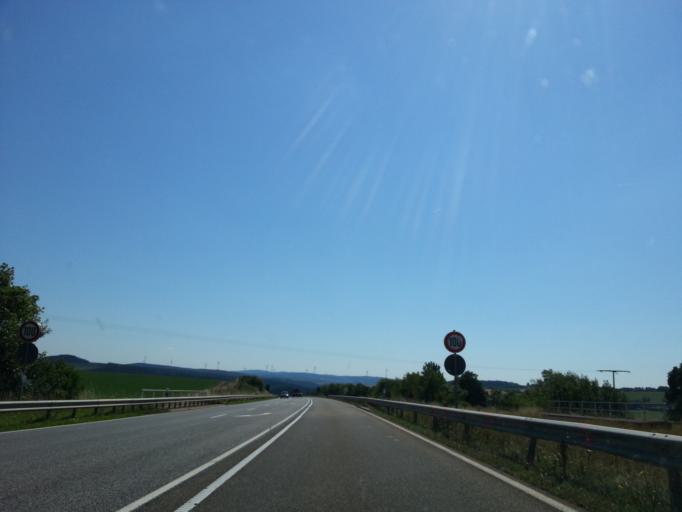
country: DE
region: Rheinland-Pfalz
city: Habscheid
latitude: 50.1993
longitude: 6.2598
